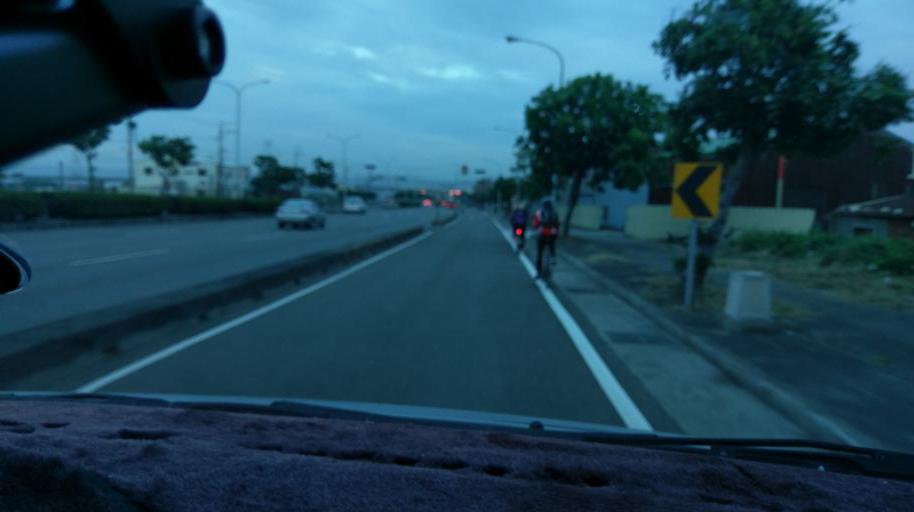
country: TW
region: Taiwan
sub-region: Changhua
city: Chang-hua
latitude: 24.2009
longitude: 120.5082
